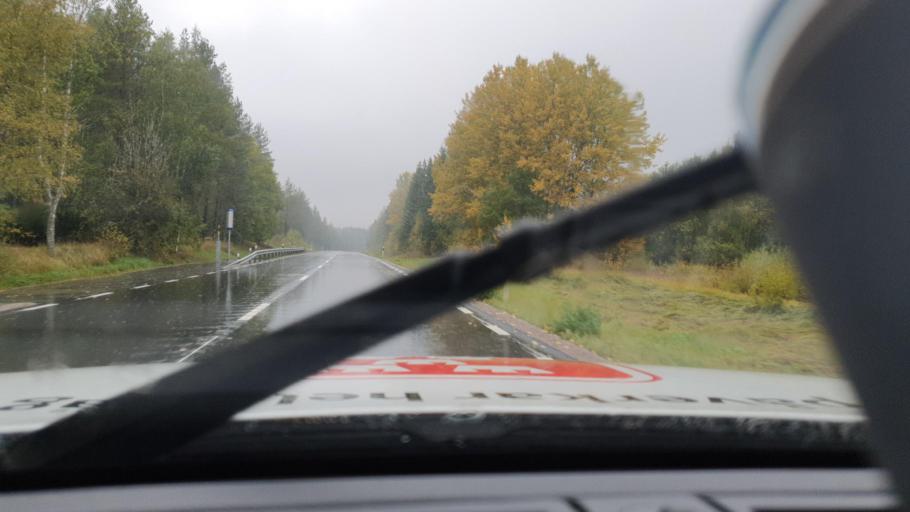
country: SE
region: Uppsala
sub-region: Tierps Kommun
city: Orbyhus
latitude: 60.2588
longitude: 17.6275
